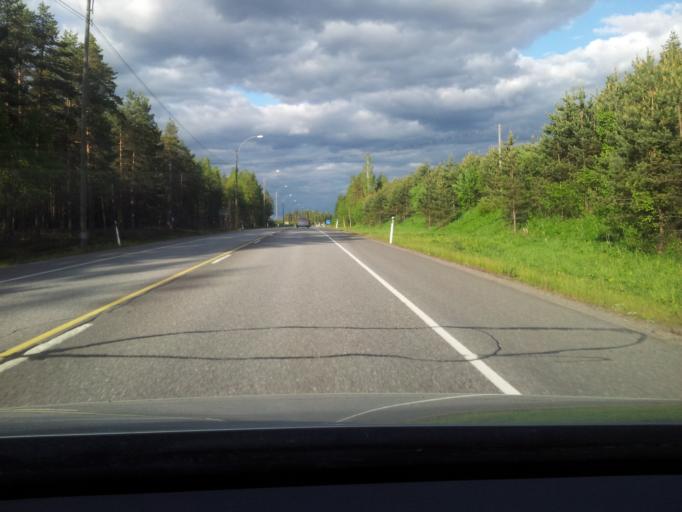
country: FI
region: South Karelia
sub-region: Lappeenranta
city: Taavetti
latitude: 60.9265
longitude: 27.5681
